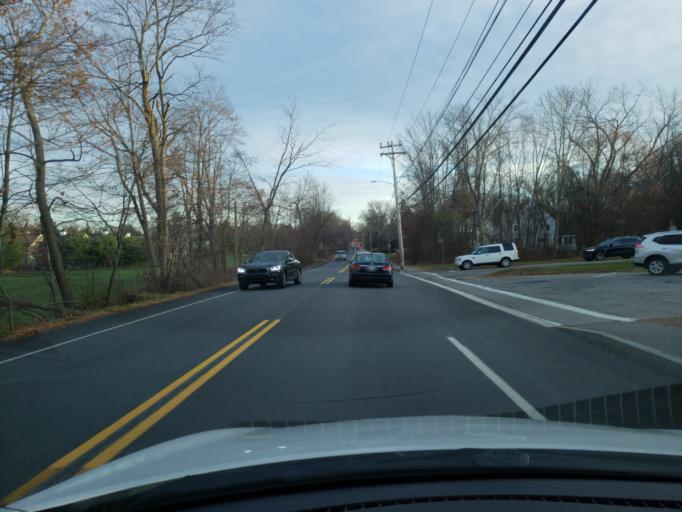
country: US
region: Massachusetts
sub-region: Essex County
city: Andover
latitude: 42.6645
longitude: -71.1702
